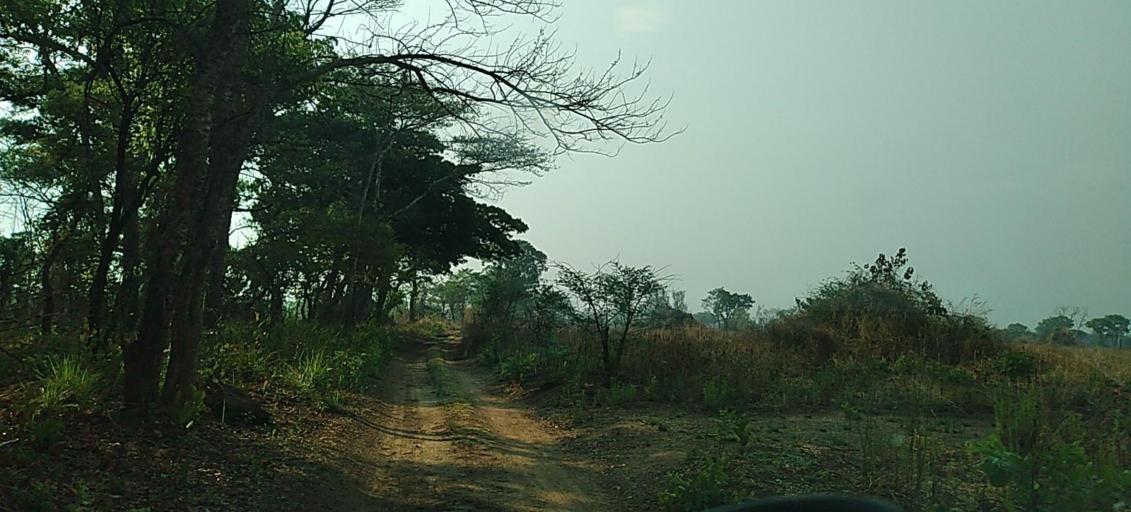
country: ZM
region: North-Western
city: Solwezi
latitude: -12.3763
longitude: 26.5623
